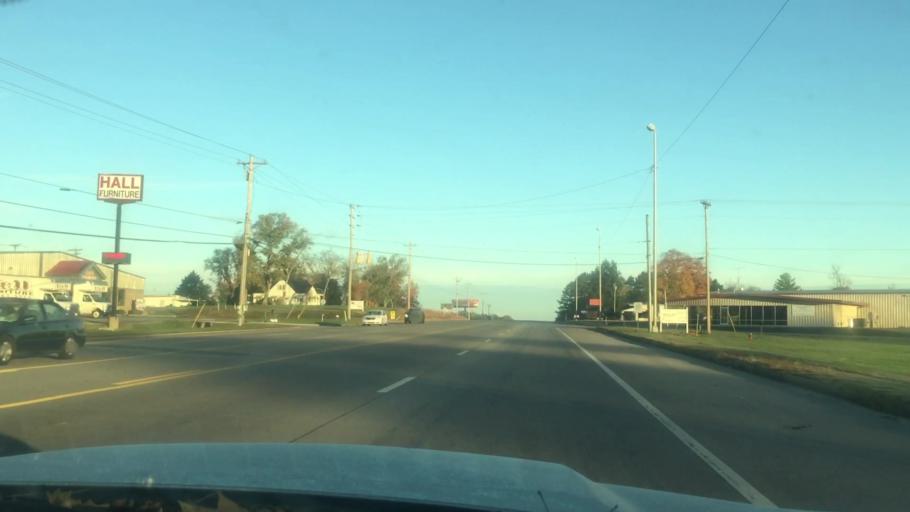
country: US
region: Tennessee
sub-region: Franklin County
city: Decherd
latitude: 35.2236
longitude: -86.1037
